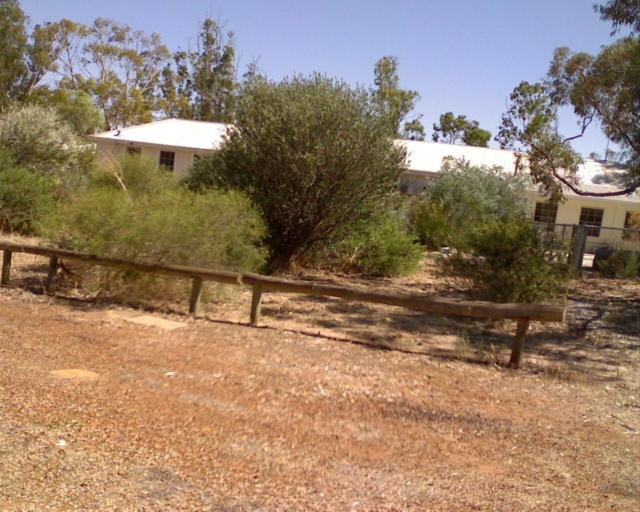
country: AU
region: Western Australia
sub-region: Moora
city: Moora
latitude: -30.2997
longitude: 116.0604
